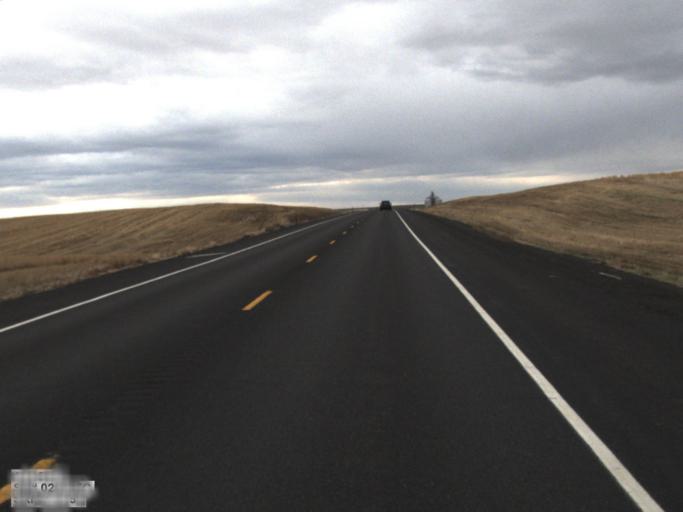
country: US
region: Washington
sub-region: Adams County
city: Ritzville
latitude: 46.7955
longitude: -118.4650
